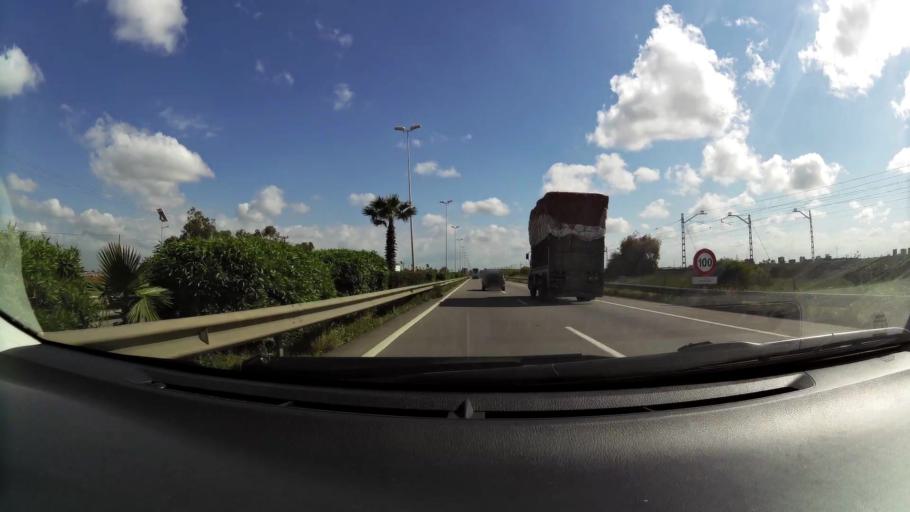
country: MA
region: Chaouia-Ouardigha
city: Nouaseur
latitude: 33.4171
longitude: -7.6267
